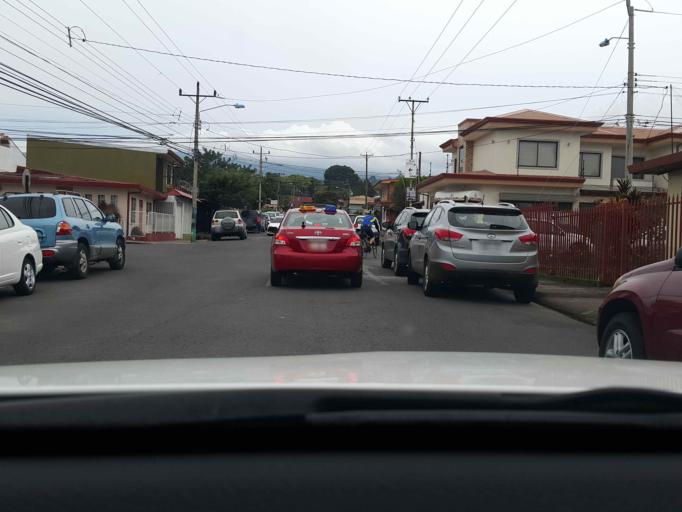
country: CR
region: Heredia
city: San Rafael
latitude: 10.0147
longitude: -84.0966
